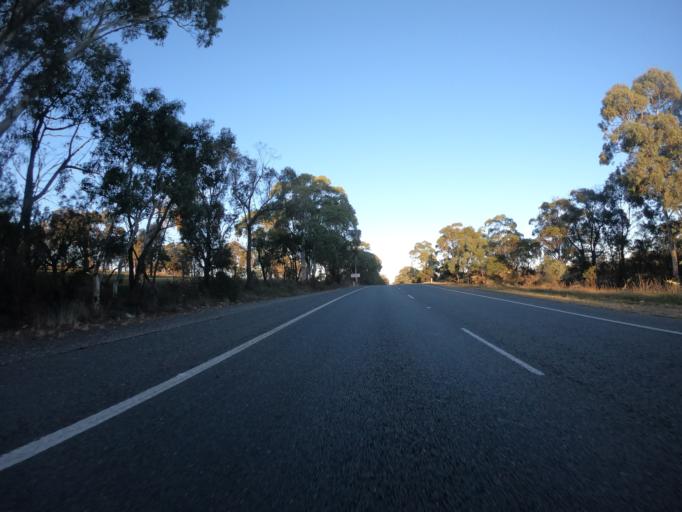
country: AU
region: New South Wales
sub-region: Goulburn Mulwaree
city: Goulburn
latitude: -34.8346
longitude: 149.5863
